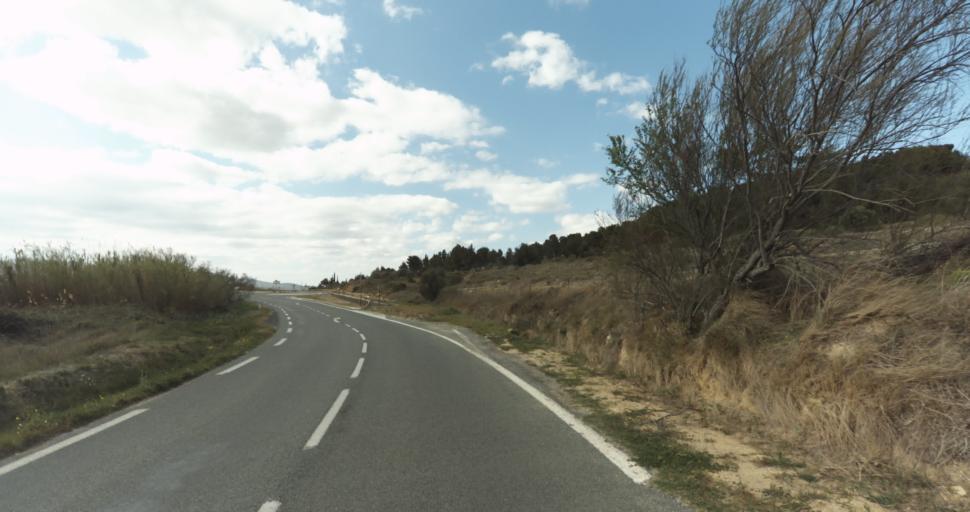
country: FR
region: Languedoc-Roussillon
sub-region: Departement de l'Aude
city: Leucate
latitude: 42.9273
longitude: 3.0136
